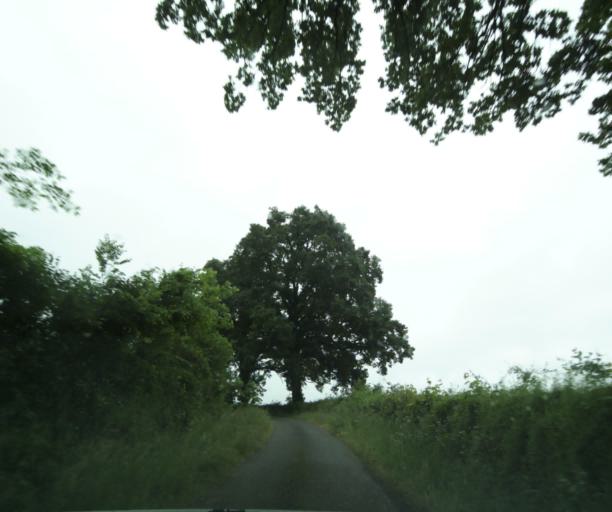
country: FR
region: Bourgogne
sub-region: Departement de Saone-et-Loire
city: La Clayette
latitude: 46.3543
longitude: 4.3623
